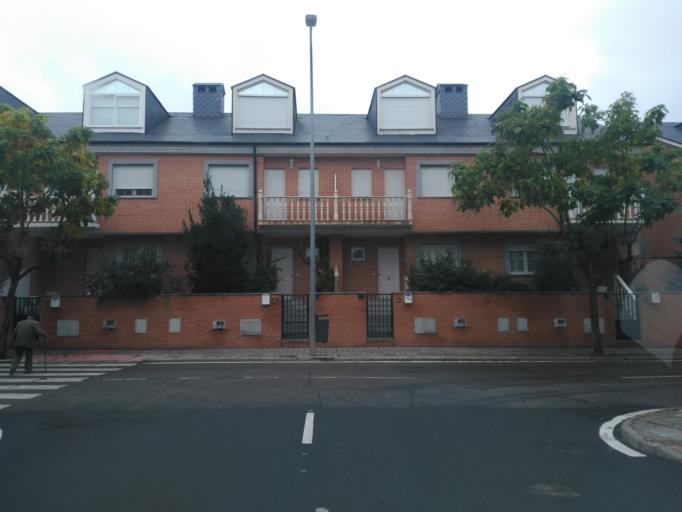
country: ES
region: Castille and Leon
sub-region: Provincia de Salamanca
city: Salamanca
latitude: 40.9555
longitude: -5.6892
